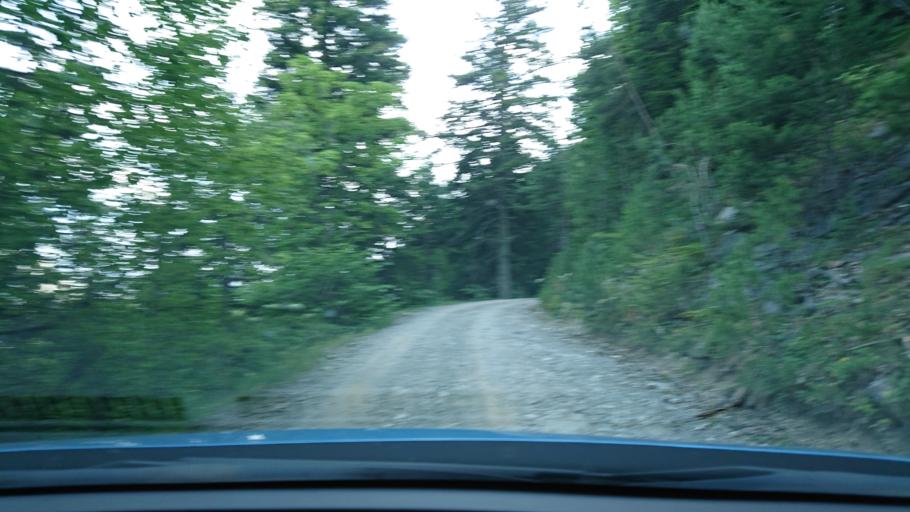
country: FR
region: Rhone-Alpes
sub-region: Departement de l'Isere
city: Mens
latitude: 44.7931
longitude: 5.8868
